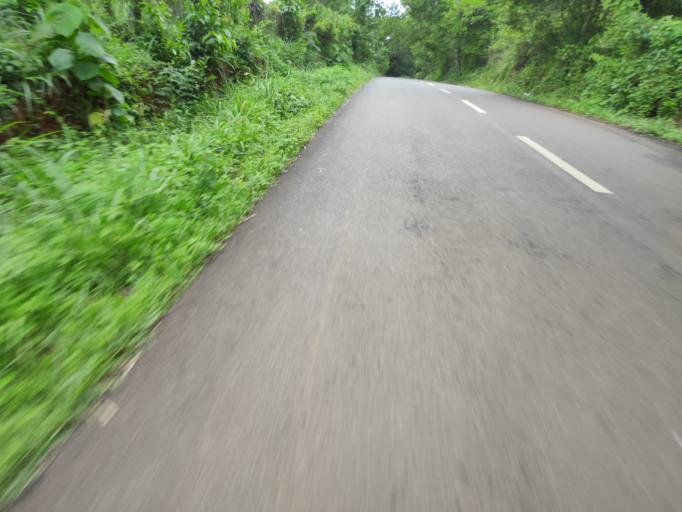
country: IN
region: Kerala
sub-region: Malappuram
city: Manjeri
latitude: 11.1709
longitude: 76.1822
